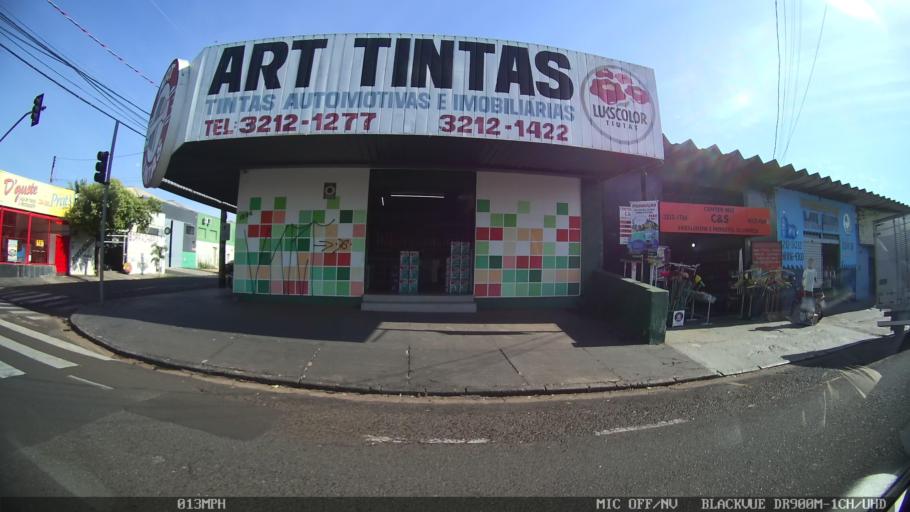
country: BR
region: Sao Paulo
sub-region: Sao Jose Do Rio Preto
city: Sao Jose do Rio Preto
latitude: -20.8034
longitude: -49.3934
